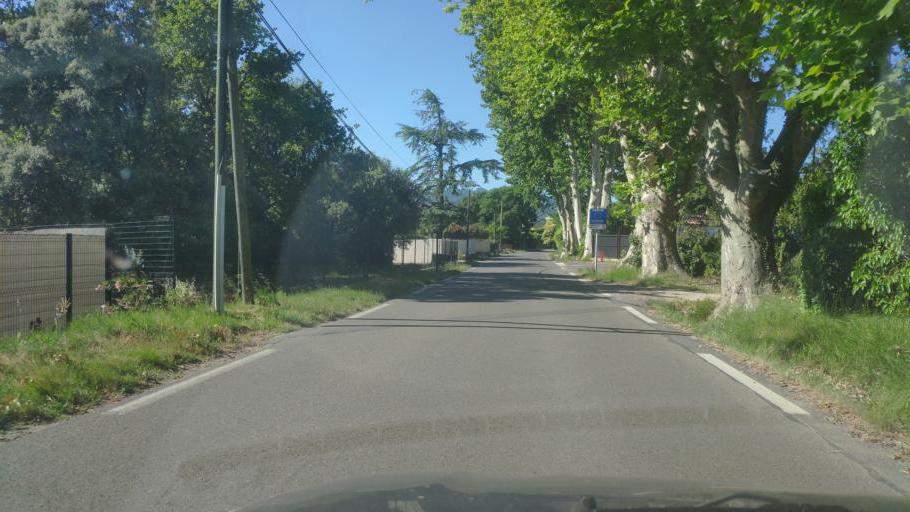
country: FR
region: Provence-Alpes-Cote d'Azur
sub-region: Departement du Vaucluse
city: Aubignan
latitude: 44.0921
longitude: 5.0256
